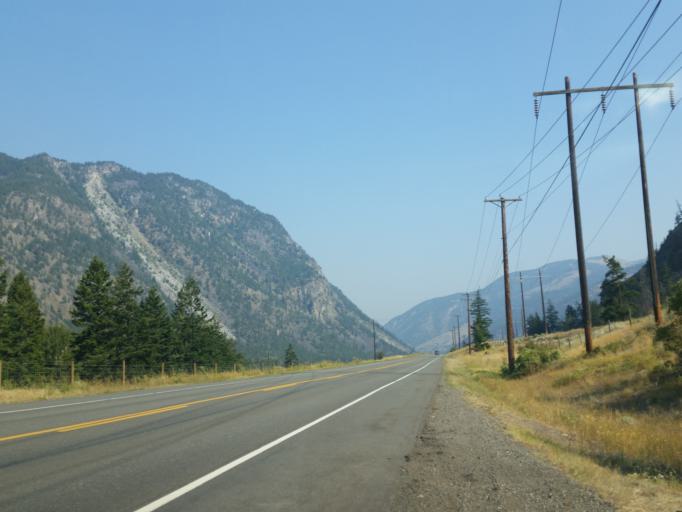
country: CA
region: British Columbia
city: Summerland
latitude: 49.2818
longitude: -120.0271
